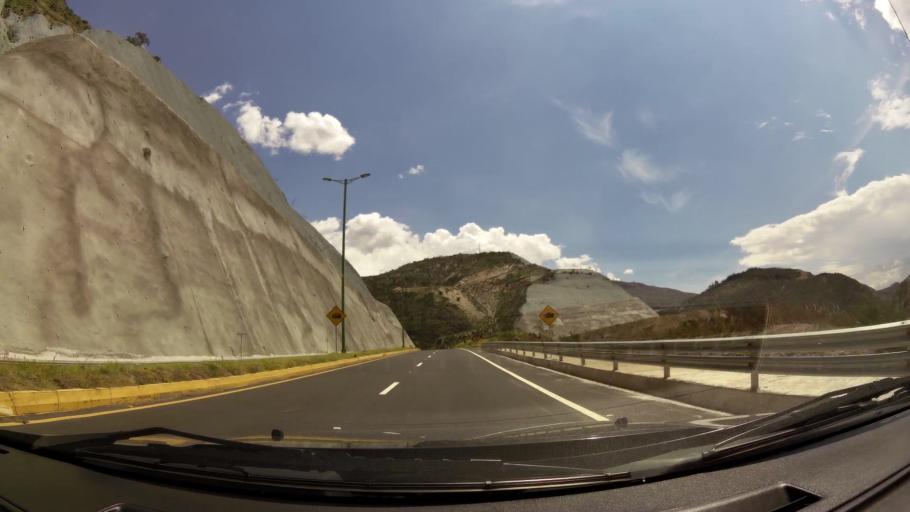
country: EC
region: Pichincha
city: Quito
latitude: -0.1038
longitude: -78.3871
